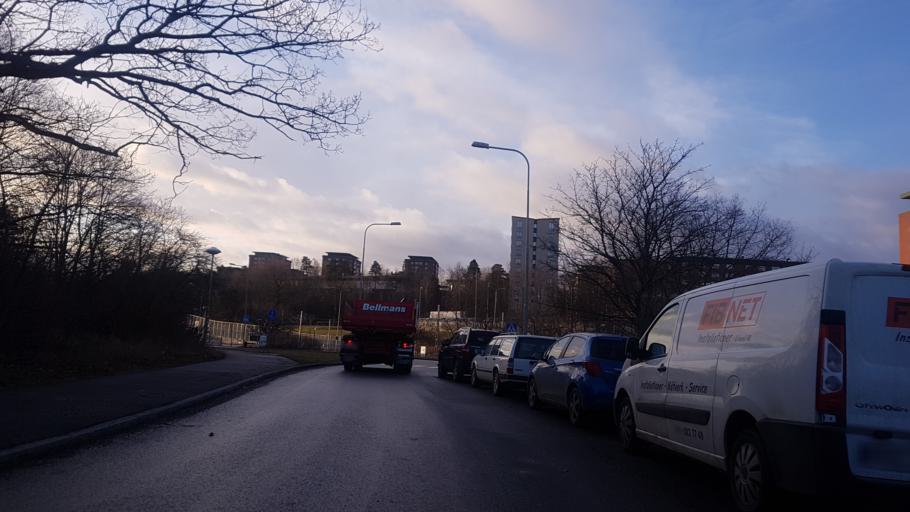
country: SE
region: Stockholm
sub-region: Lidingo
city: Lidingoe
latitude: 59.3505
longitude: 18.1491
